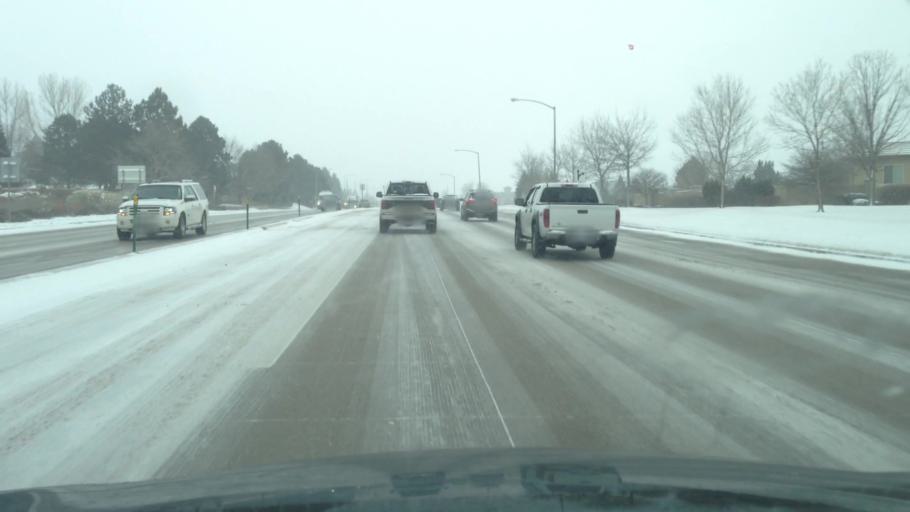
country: US
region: Colorado
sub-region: Arapahoe County
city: Dove Valley
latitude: 39.6300
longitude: -104.8252
